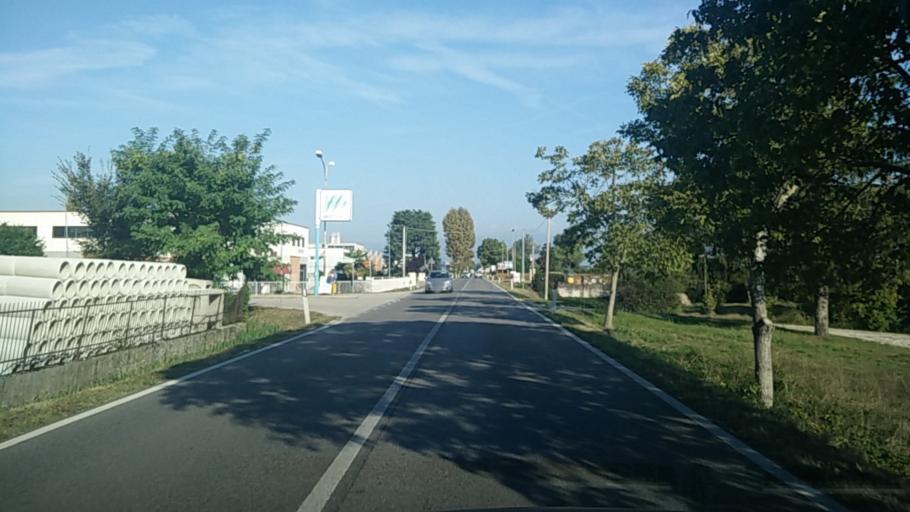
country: IT
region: Veneto
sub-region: Provincia di Treviso
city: Resana
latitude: 45.6474
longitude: 11.9467
